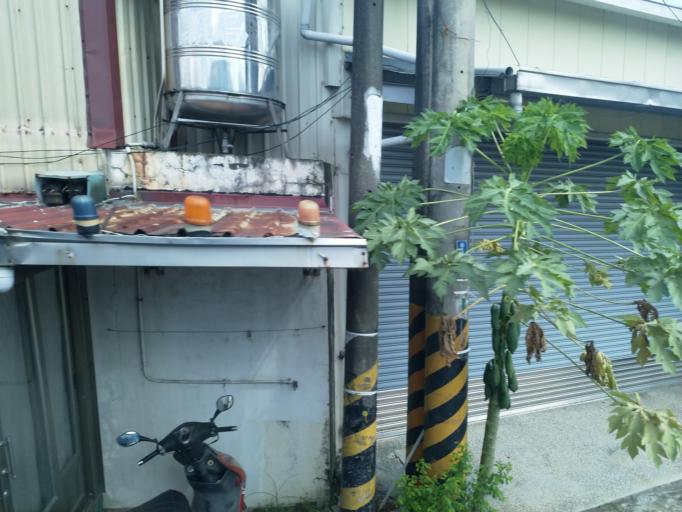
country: TW
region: Taiwan
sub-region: Pingtung
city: Pingtung
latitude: 22.8929
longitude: 120.5496
